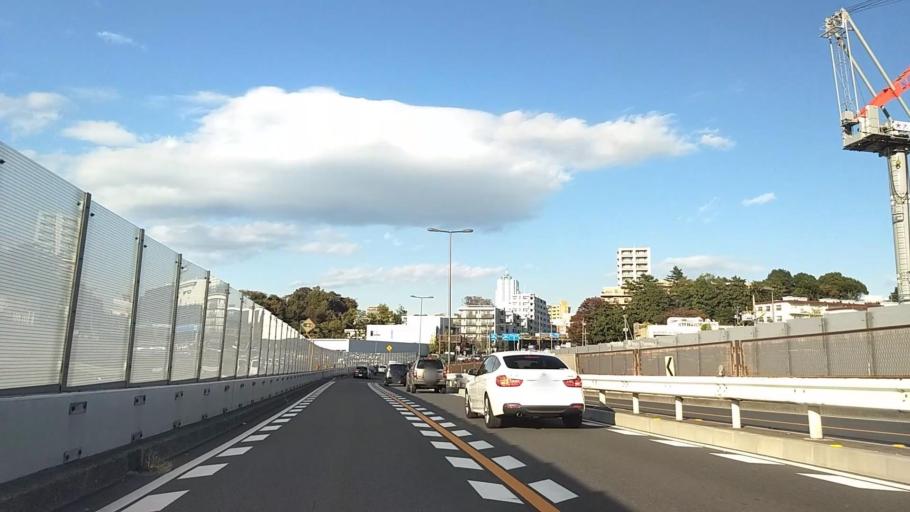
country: JP
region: Tokyo
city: Chofugaoka
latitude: 35.6168
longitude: 139.6279
